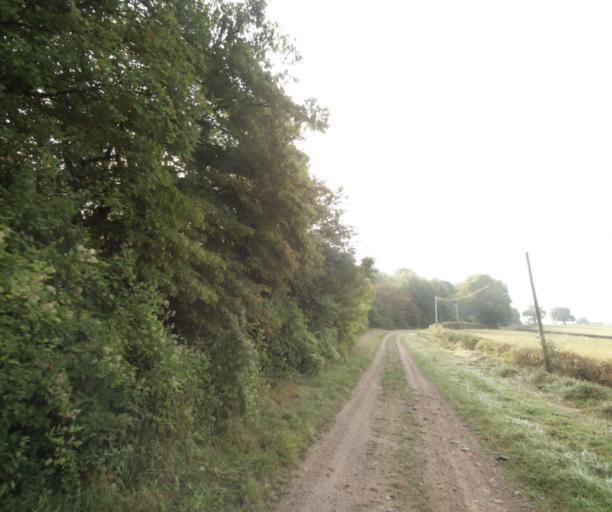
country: FR
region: Bourgogne
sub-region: Departement de Saone-et-Loire
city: Charolles
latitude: 46.4757
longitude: 4.2761
